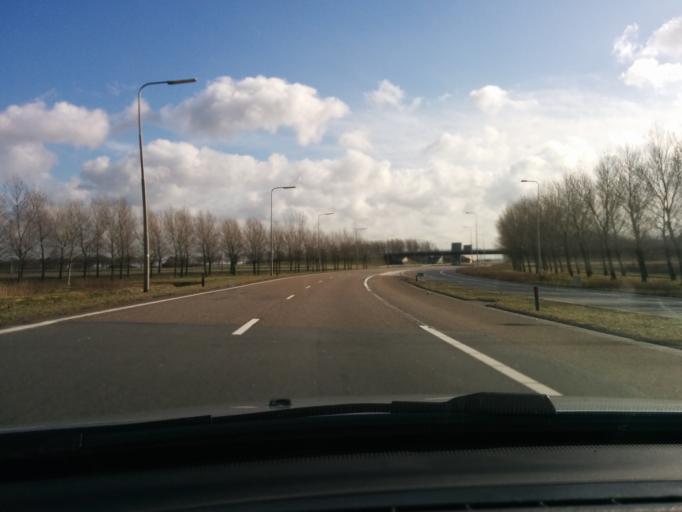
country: NL
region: Flevoland
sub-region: Gemeente Almere
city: Almere Stad
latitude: 52.3785
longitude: 5.3018
